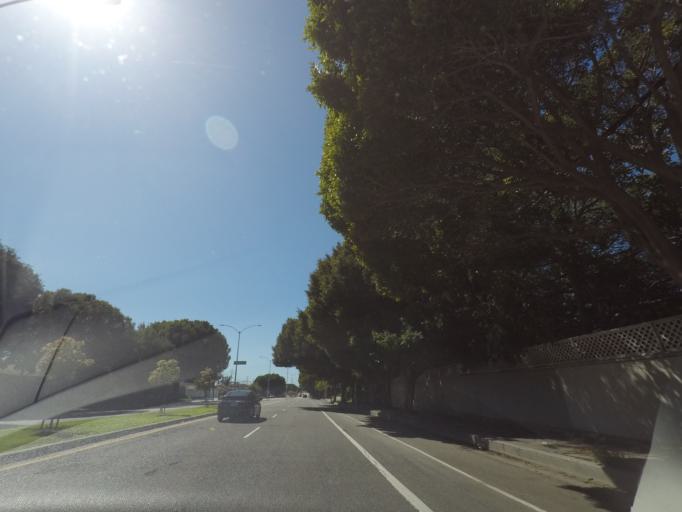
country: US
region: California
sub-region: Los Angeles County
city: Ladera Heights
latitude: 33.9600
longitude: -118.3993
